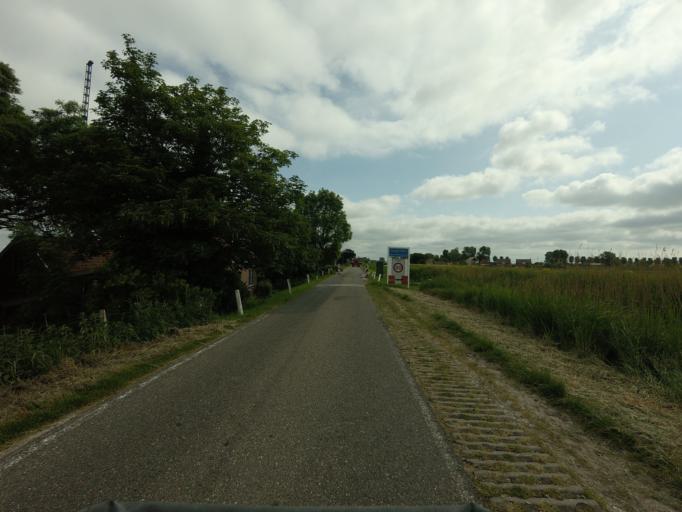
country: NL
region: North Holland
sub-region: Gemeente Zaanstad
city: Zaanstad
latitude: 52.5370
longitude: 4.8296
